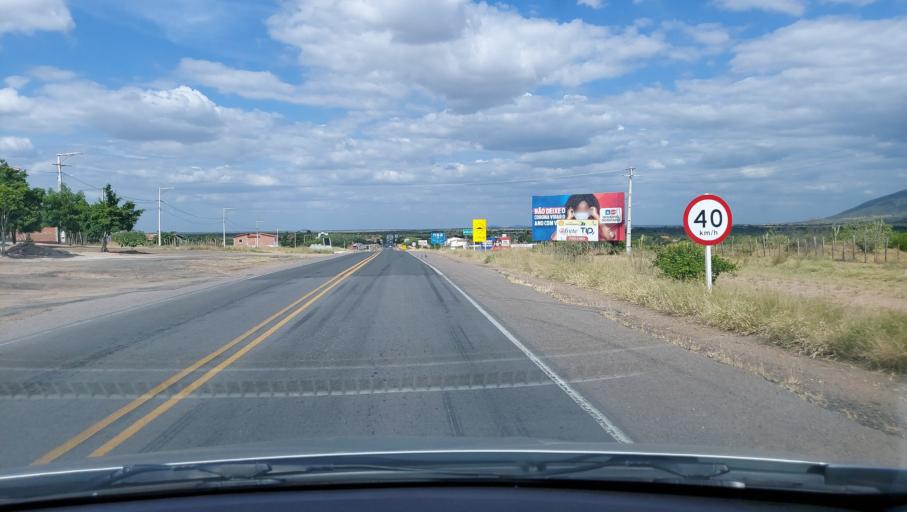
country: BR
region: Bahia
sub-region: Itaberaba
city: Itaberaba
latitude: -12.5182
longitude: -39.9432
